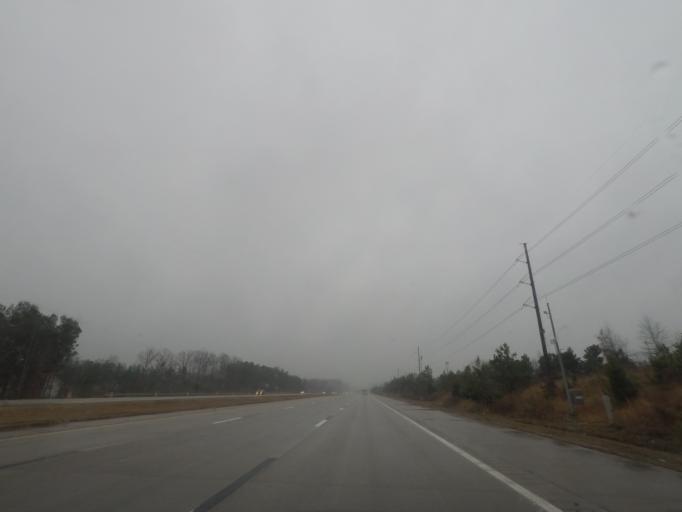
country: US
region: North Carolina
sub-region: Wake County
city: Green Level
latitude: 35.8010
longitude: -78.8910
